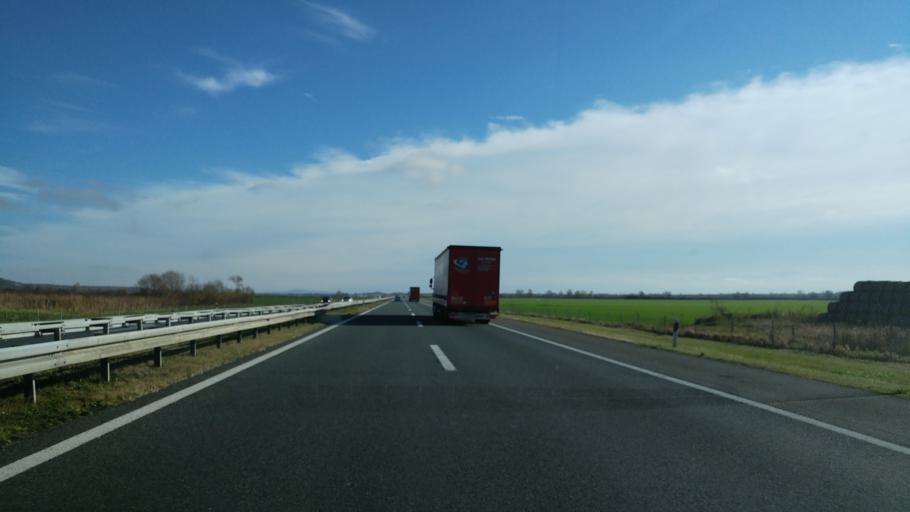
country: HR
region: Brodsko-Posavska
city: Okucani
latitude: 45.2765
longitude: 17.1253
